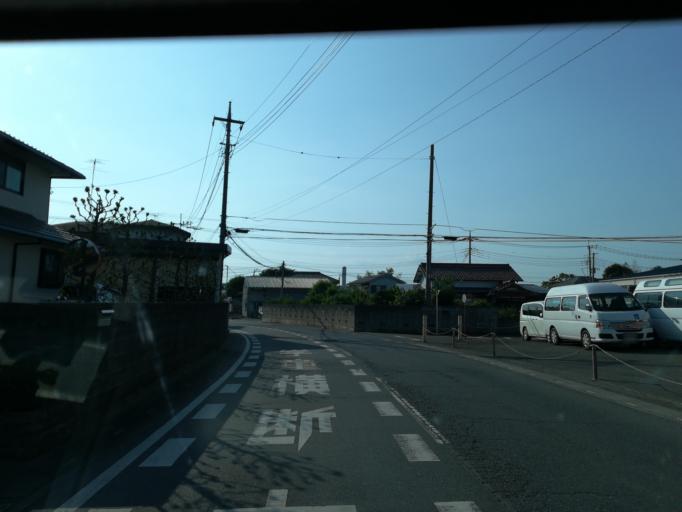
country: JP
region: Saitama
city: Sayama
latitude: 35.8009
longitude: 139.3915
